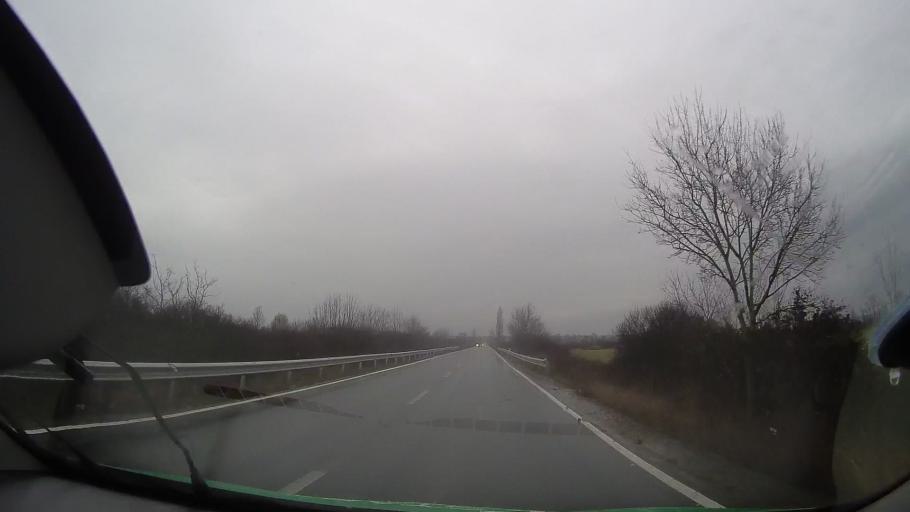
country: RO
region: Bihor
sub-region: Comuna Tinca
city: Tinca
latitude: 46.7443
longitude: 21.9392
